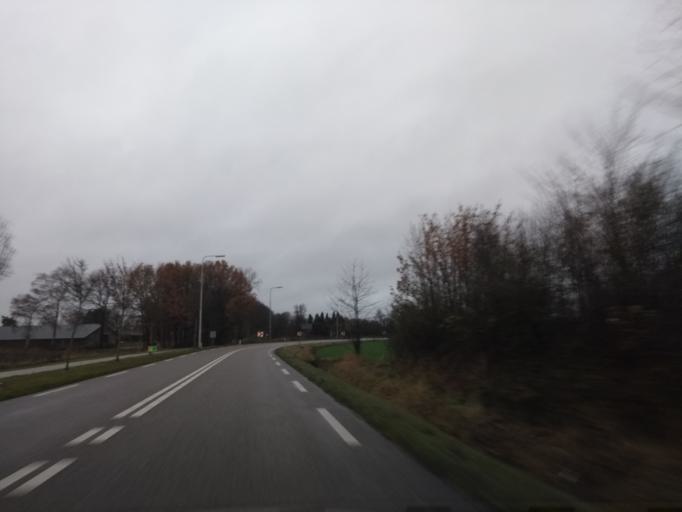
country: NL
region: Limburg
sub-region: Gemeente Weert
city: Weert
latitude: 51.2255
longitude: 5.7190
